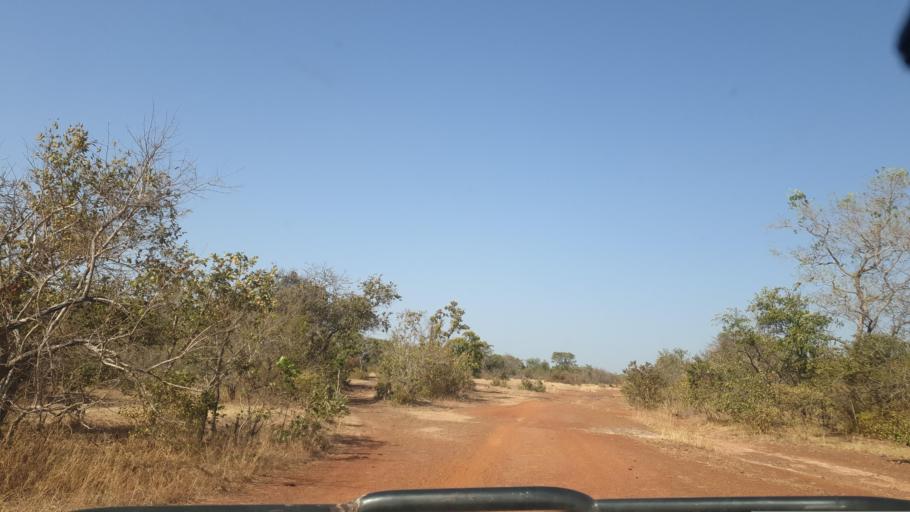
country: ML
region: Sikasso
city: Bougouni
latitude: 11.8192
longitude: -6.9476
